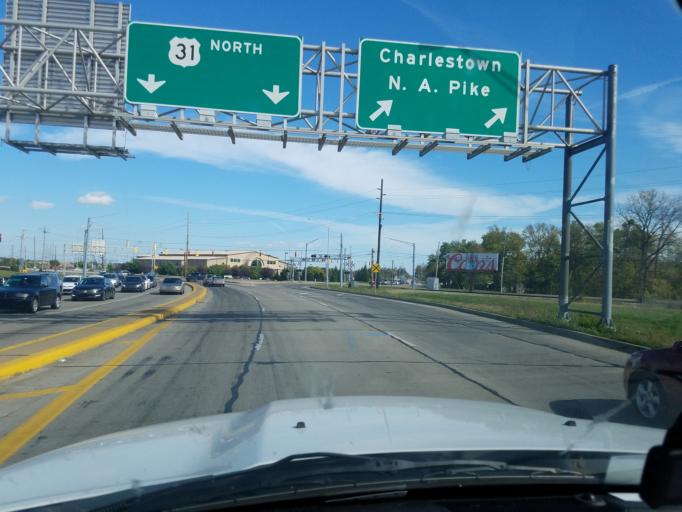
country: US
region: Indiana
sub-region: Clark County
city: Clarksville
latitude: 38.3195
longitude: -85.7523
